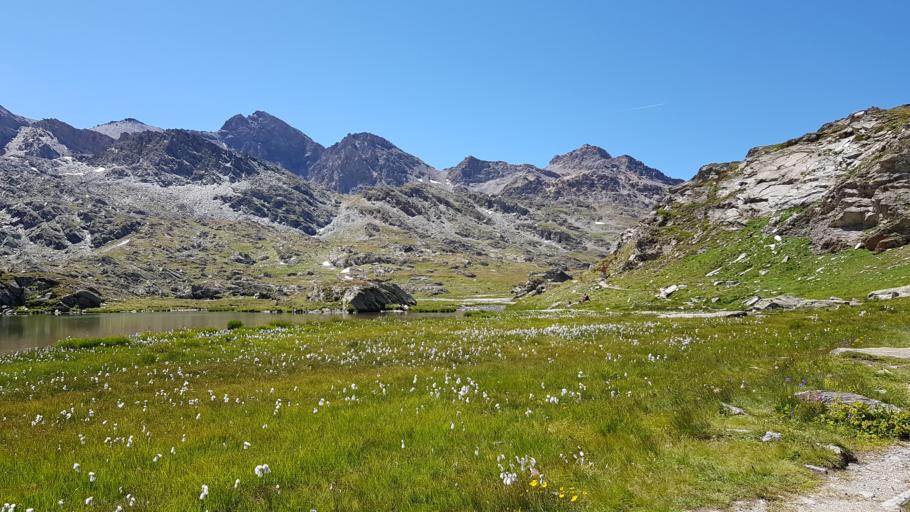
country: IT
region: Piedmont
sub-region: Provincia di Cuneo
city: Pontechianale
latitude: 44.6431
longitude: 6.9549
